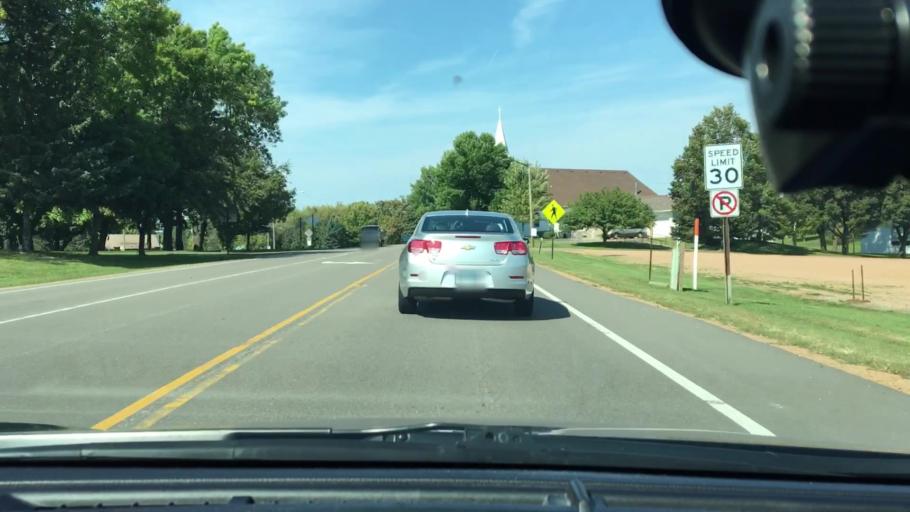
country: US
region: Minnesota
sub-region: Hennepin County
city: Corcoran
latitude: 45.0940
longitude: -93.5436
